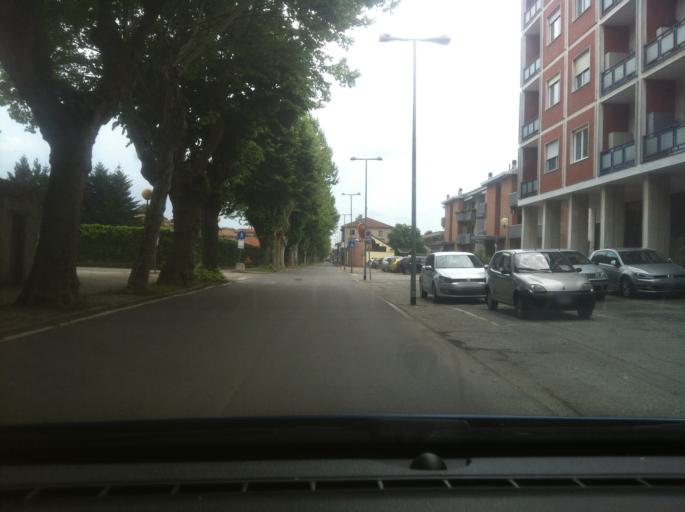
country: IT
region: Piedmont
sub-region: Provincia di Torino
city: Romano Canavese
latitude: 45.3860
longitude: 7.8700
